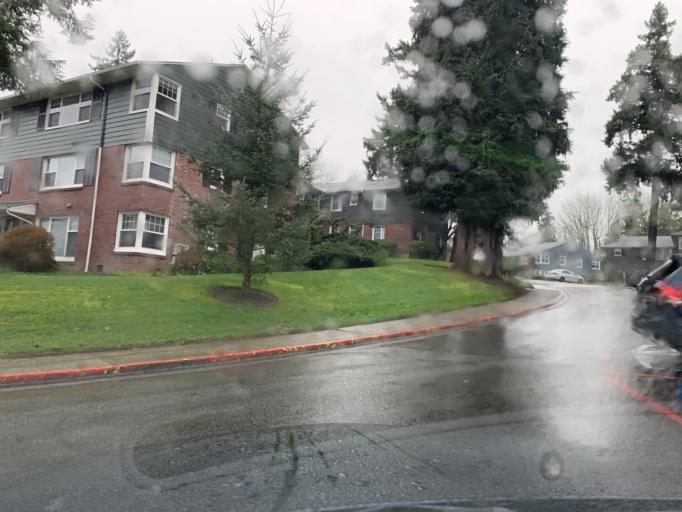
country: US
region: Washington
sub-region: King County
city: Mercer Island
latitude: 47.5806
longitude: -122.2216
